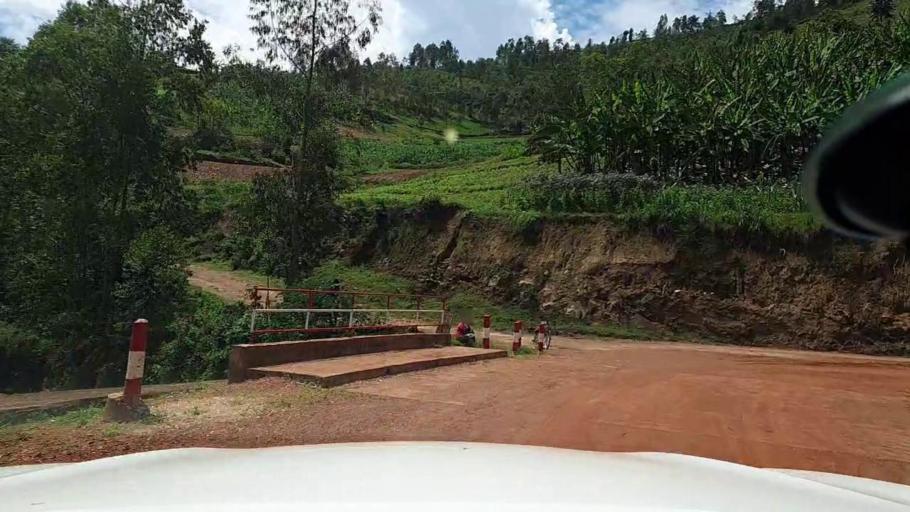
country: RW
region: Northern Province
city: Musanze
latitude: -1.6951
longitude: 29.8207
